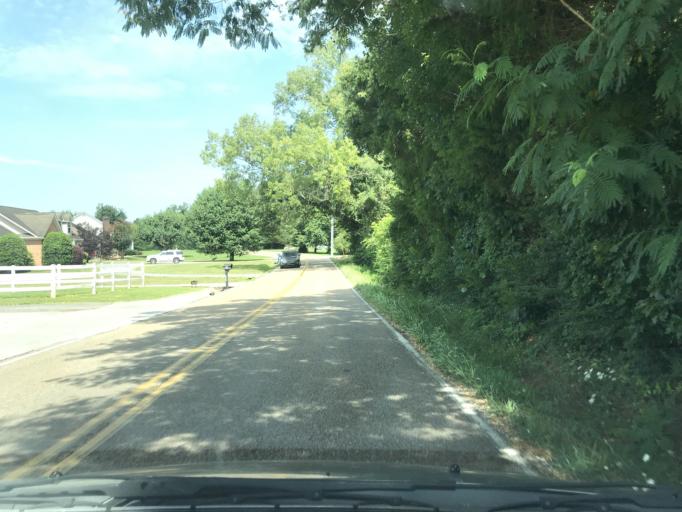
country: US
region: Tennessee
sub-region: Hamilton County
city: Lakesite
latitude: 35.1678
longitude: -85.0613
